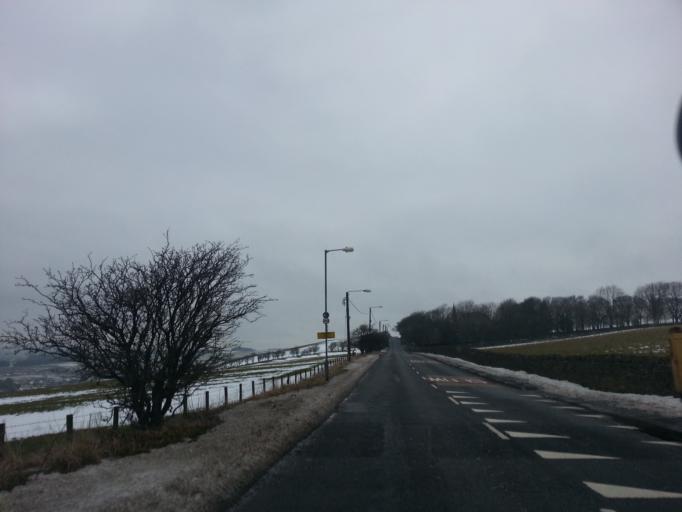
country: GB
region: England
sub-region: County Durham
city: Crook
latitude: 54.7357
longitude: -1.7504
